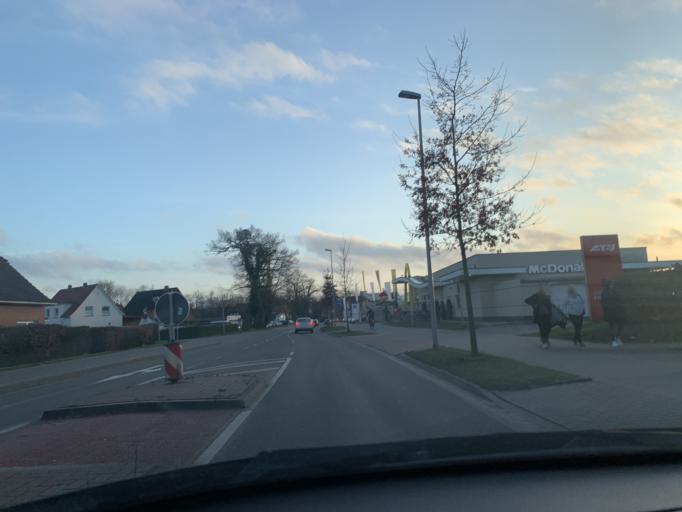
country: DE
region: Lower Saxony
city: Oldenburg
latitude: 53.1722
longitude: 8.2298
